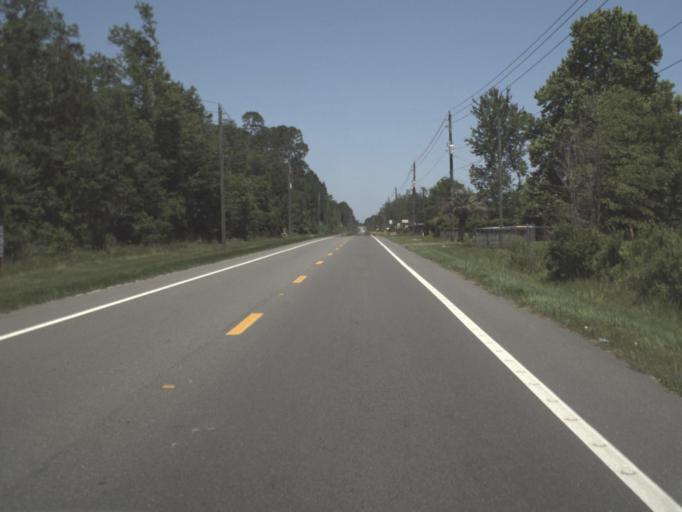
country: US
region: Florida
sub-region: Baker County
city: Macclenny
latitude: 30.2850
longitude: -82.1068
